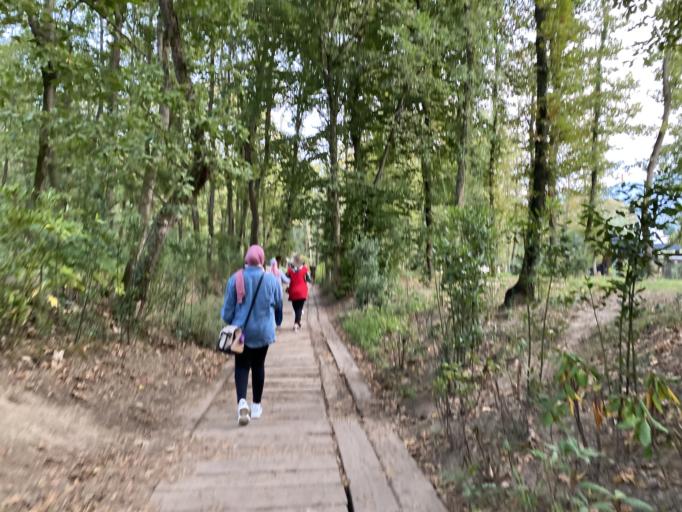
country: TR
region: Kocaeli
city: Derbent
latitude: 40.7337
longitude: 30.1624
